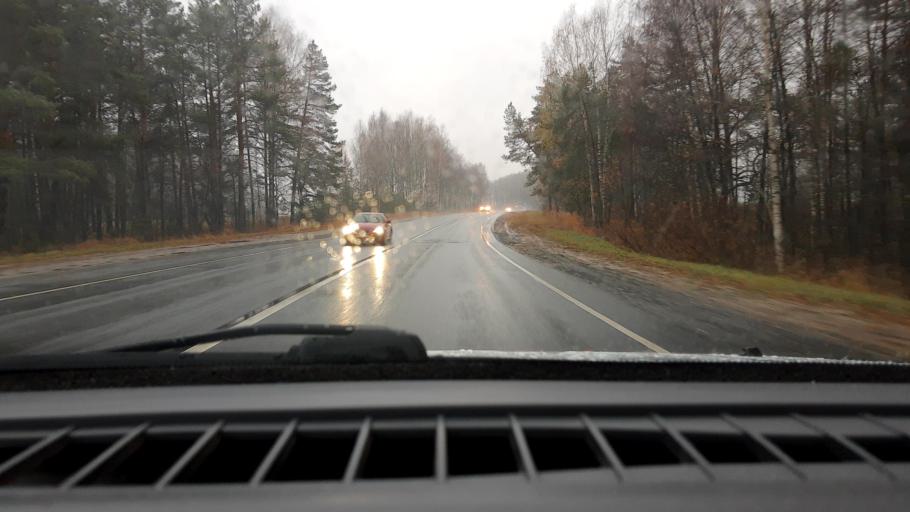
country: RU
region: Nizjnij Novgorod
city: Linda
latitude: 56.6602
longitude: 44.1275
